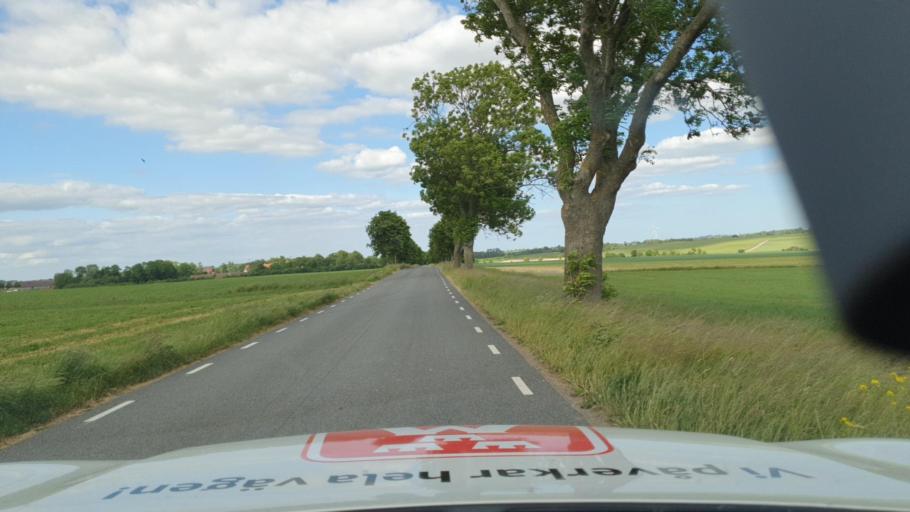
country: SE
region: Skane
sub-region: Tomelilla Kommun
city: Tomelilla
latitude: 55.4851
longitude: 14.0353
